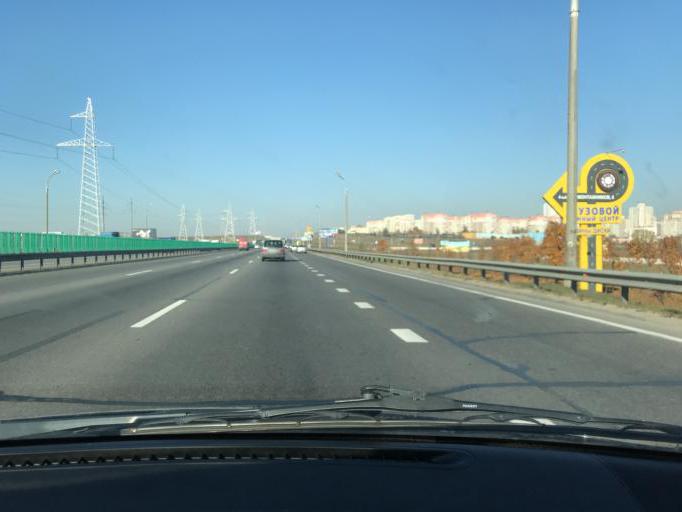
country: BY
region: Minsk
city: Malinovka
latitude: 53.8740
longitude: 27.4206
